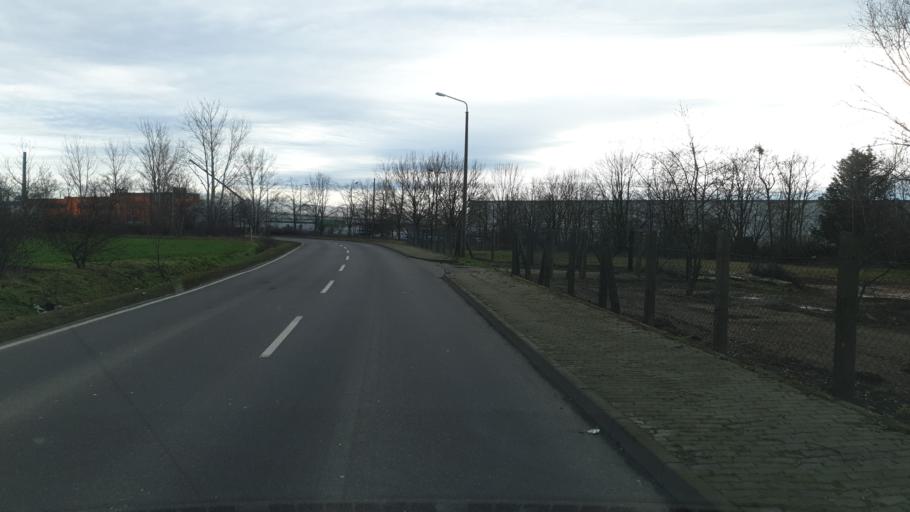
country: DE
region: Saxony
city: Kitzen
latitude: 51.2511
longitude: 12.2629
